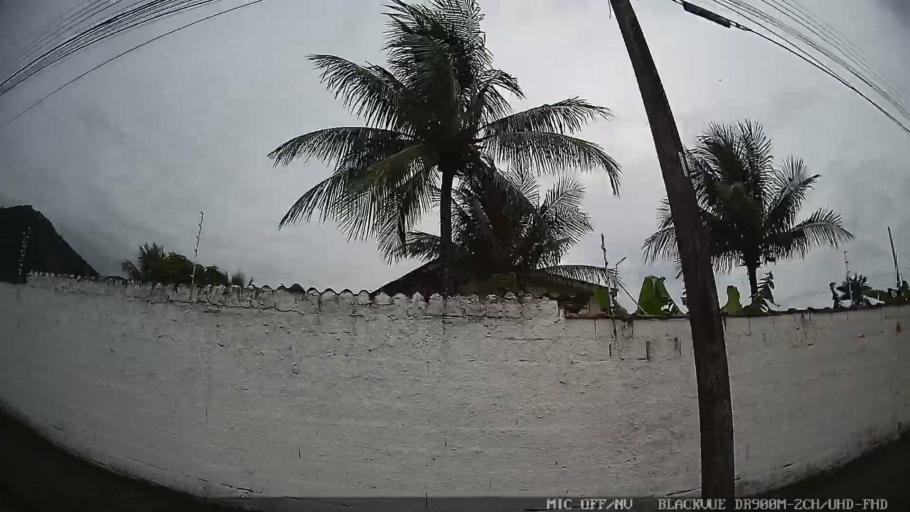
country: BR
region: Sao Paulo
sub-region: Caraguatatuba
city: Caraguatatuba
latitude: -23.6177
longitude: -45.3921
